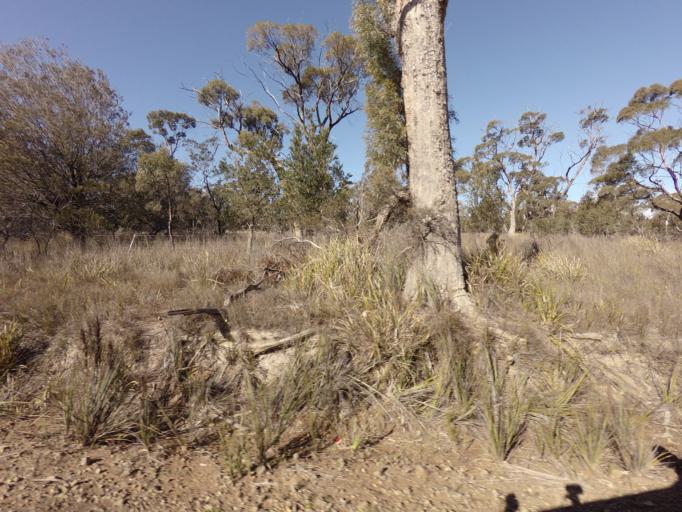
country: AU
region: Tasmania
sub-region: Sorell
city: Sorell
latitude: -42.3491
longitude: 147.9727
